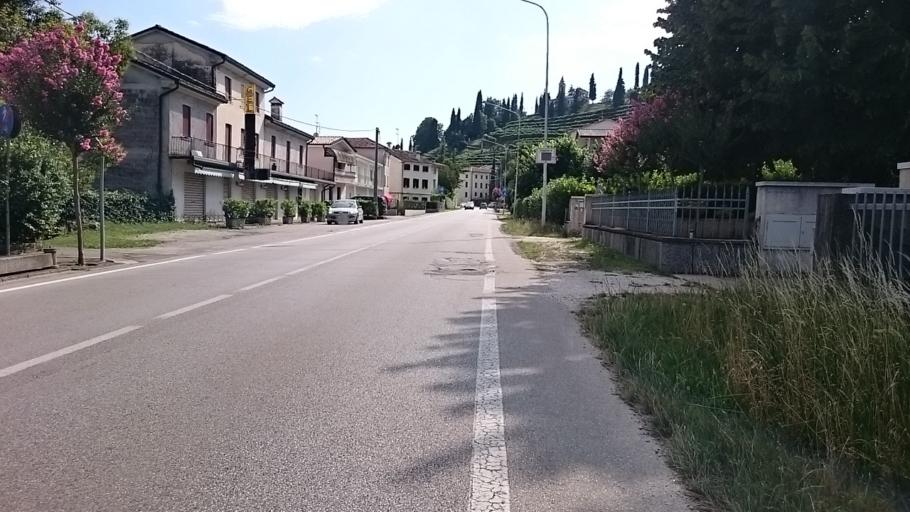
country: IT
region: Veneto
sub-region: Provincia di Treviso
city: Vidor
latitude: 45.8650
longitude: 12.0404
